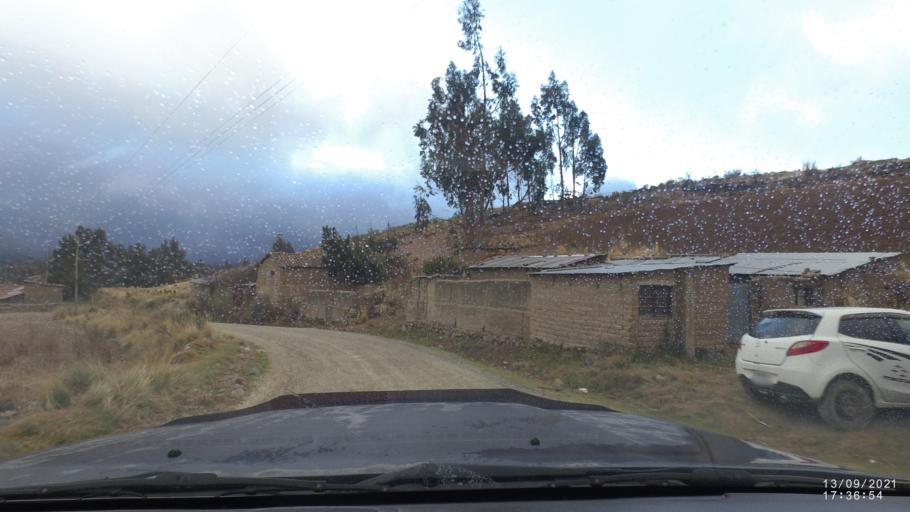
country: BO
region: Cochabamba
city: Colomi
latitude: -17.3616
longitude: -65.8025
